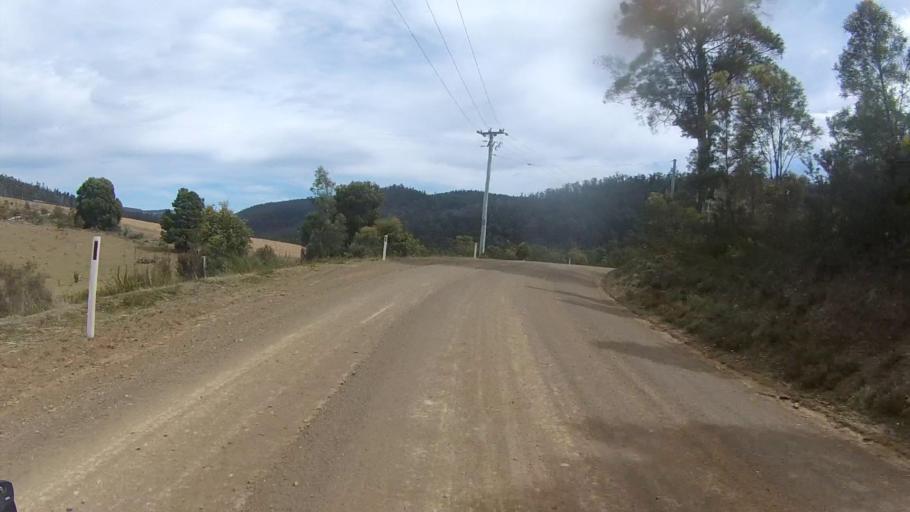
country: AU
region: Tasmania
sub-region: Sorell
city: Sorell
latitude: -42.7570
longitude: 147.7999
